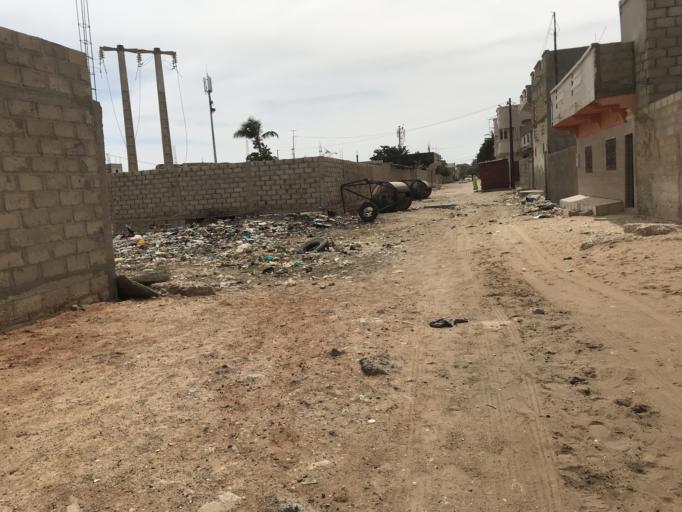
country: SN
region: Saint-Louis
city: Saint-Louis
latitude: 16.0251
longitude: -16.4824
